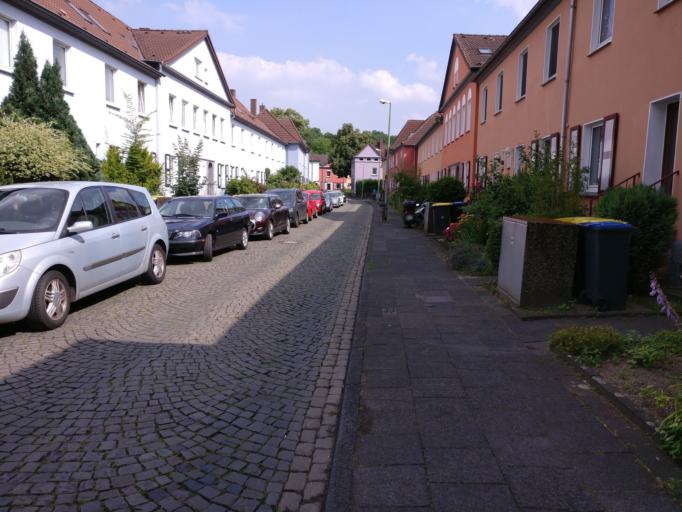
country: DE
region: North Rhine-Westphalia
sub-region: Regierungsbezirk Dusseldorf
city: Duisburg
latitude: 51.4253
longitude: 6.7933
